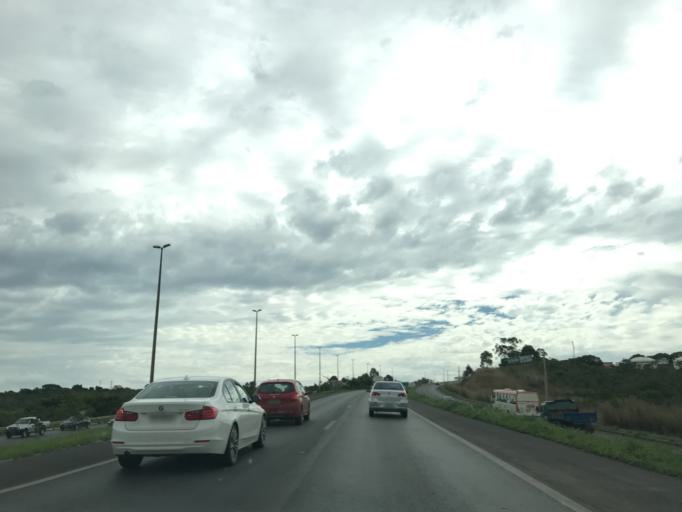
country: BR
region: Federal District
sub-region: Brasilia
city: Brasilia
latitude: -15.6771
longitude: -47.8261
